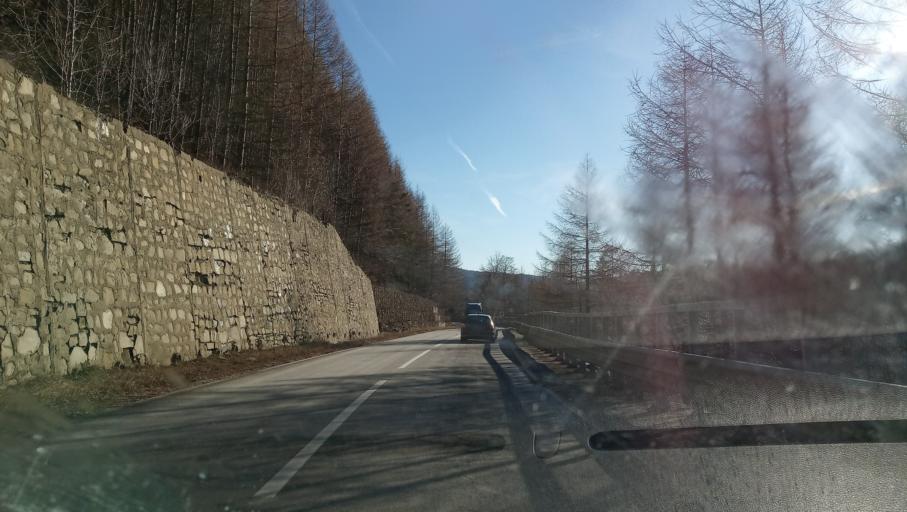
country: RO
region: Brasov
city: Crivina
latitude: 45.4713
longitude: 25.9210
